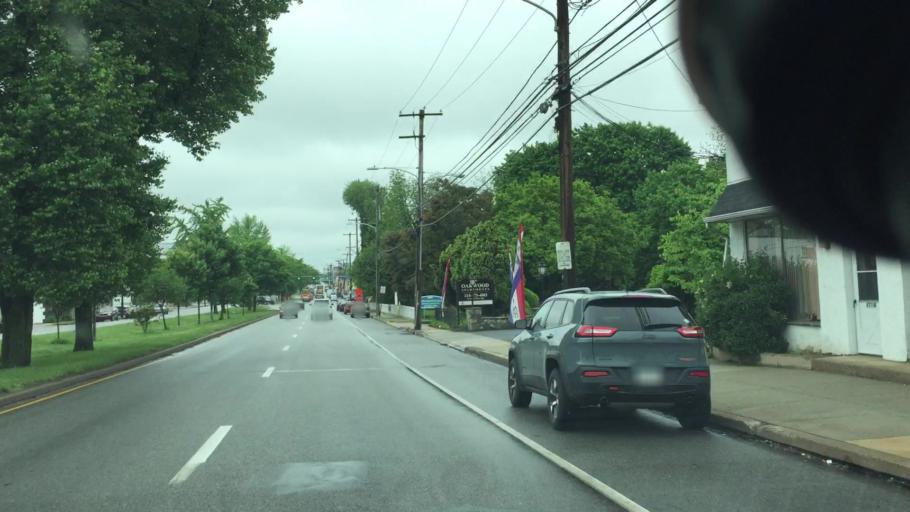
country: US
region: Pennsylvania
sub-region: Delaware County
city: Drexel Hill
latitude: 39.9672
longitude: -75.2870
